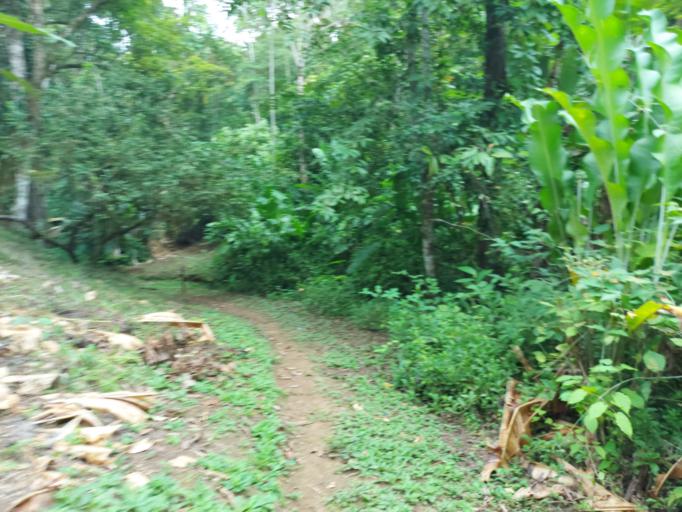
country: PA
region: Bocas del Toro
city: Barranco
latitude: 9.6426
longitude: -82.7854
